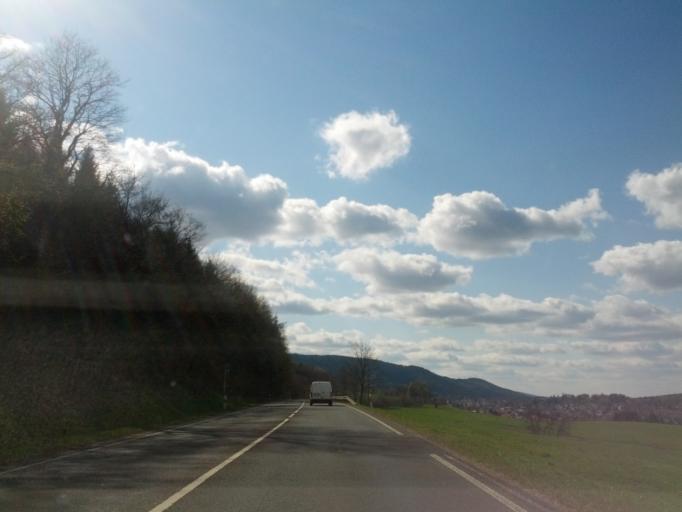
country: DE
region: Thuringia
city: Finsterbergen
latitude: 50.8526
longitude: 10.5965
